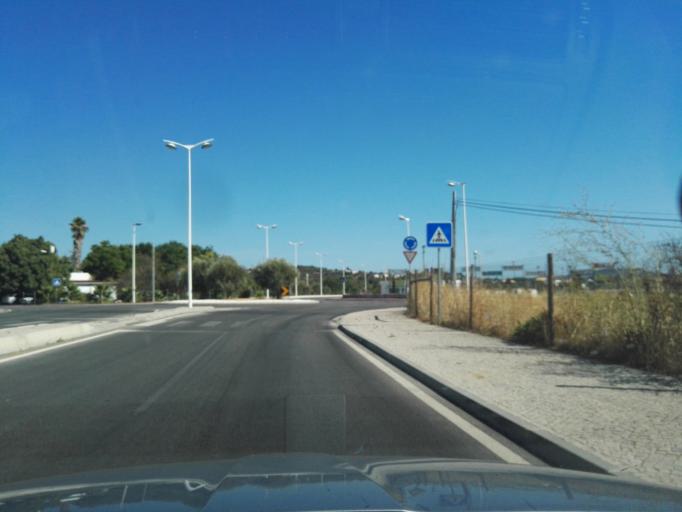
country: PT
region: Faro
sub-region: Sao Bras de Alportel
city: Sao Bras de Alportel
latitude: 37.1582
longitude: -7.8811
